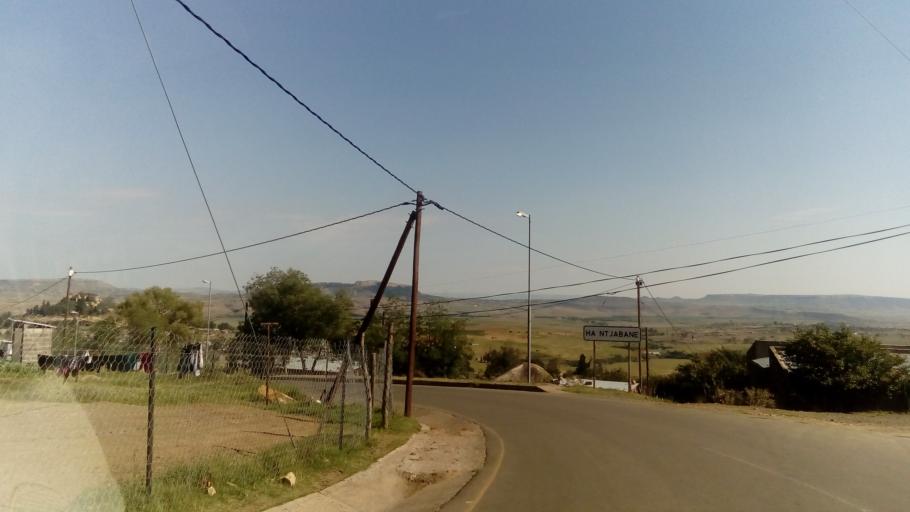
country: LS
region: Berea
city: Teyateyaneng
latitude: -29.1369
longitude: 27.7505
